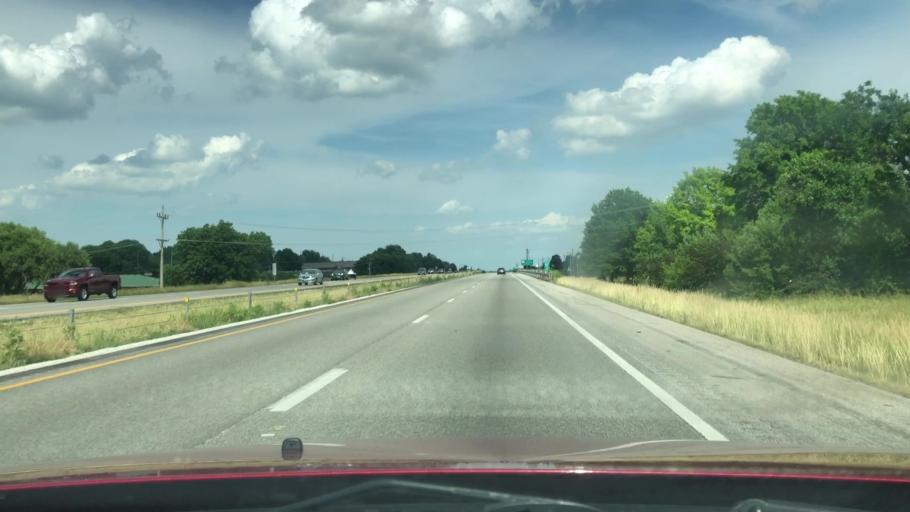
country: US
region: Missouri
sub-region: Greene County
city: Springfield
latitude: 37.2502
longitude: -93.2784
